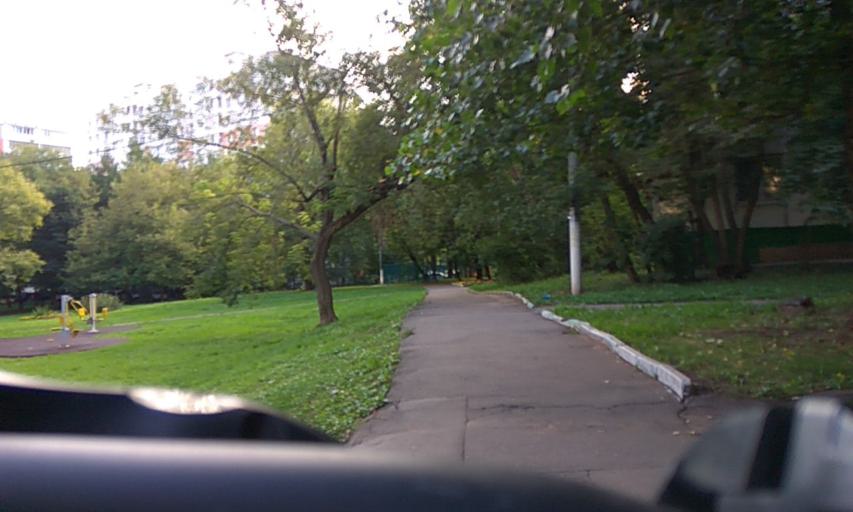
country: RU
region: Moscow
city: Kolomenskoye
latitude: 55.6776
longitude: 37.6854
